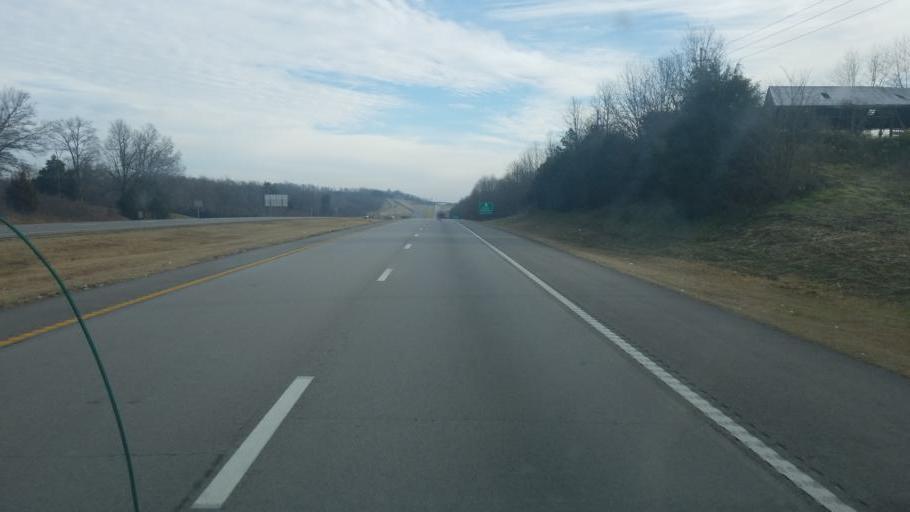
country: US
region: Missouri
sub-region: Stoddard County
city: Dexter
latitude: 36.8122
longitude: -89.9583
